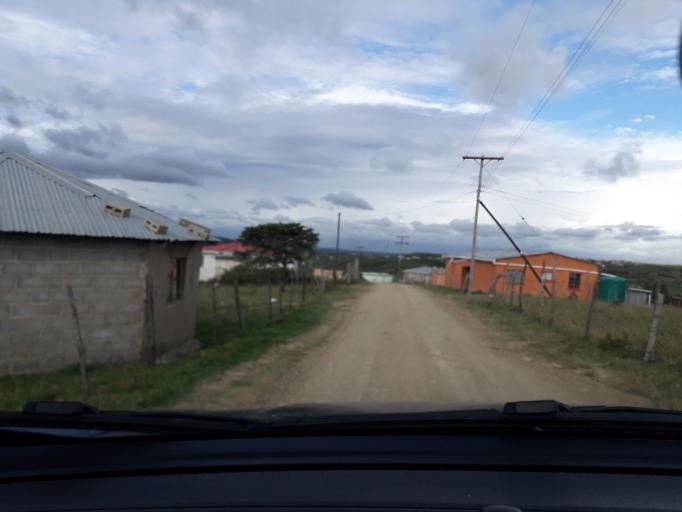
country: ZA
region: Eastern Cape
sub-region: Buffalo City Metropolitan Municipality
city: East London
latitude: -32.8055
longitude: 27.9560
